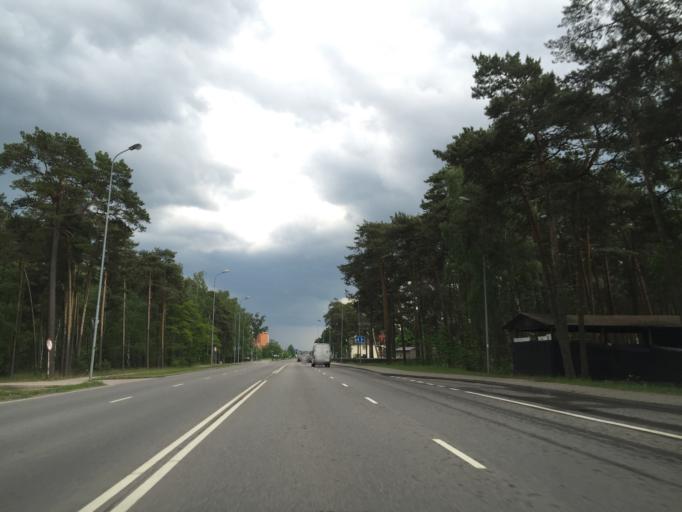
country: LT
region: Klaipedos apskritis
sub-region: Klaipeda
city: Klaipeda
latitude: 55.7317
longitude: 21.1208
